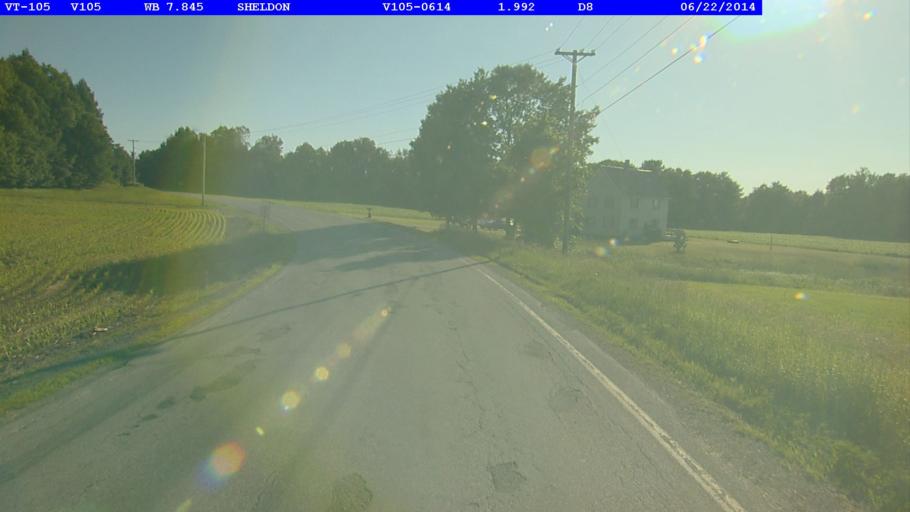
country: US
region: Vermont
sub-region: Franklin County
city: Saint Albans
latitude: 44.9046
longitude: -72.9925
